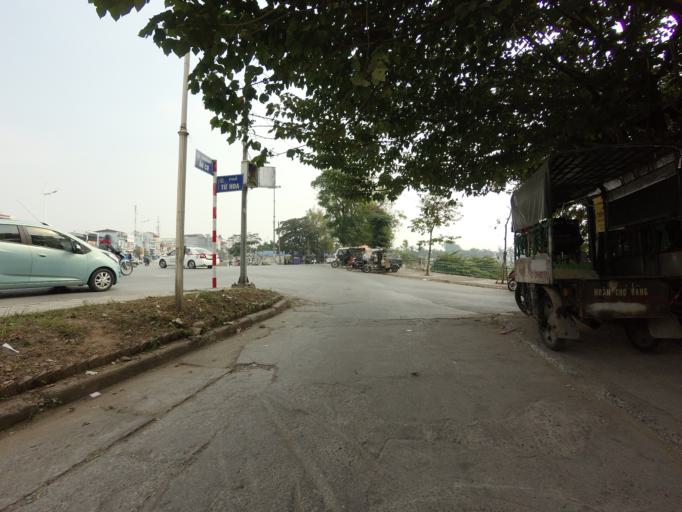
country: VN
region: Ha Noi
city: Tay Ho
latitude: 21.0591
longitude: 105.8339
